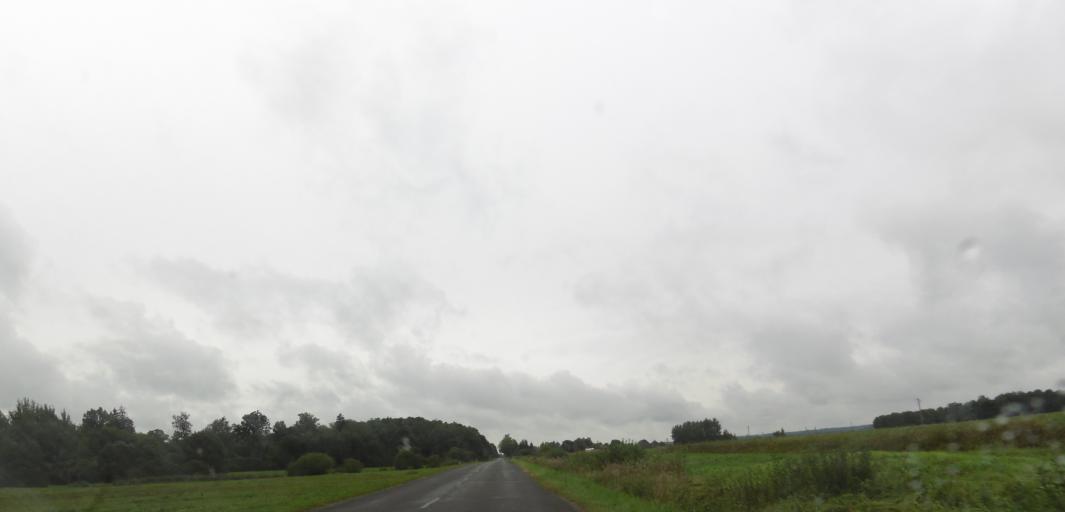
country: LT
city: Sirvintos
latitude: 55.0727
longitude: 24.9673
